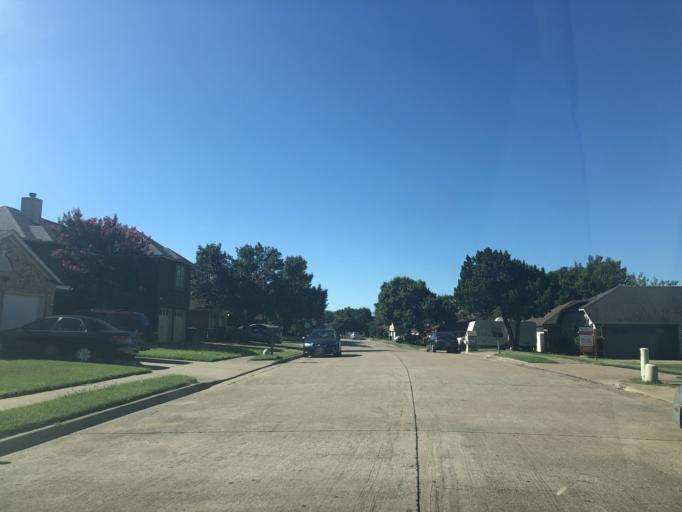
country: US
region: Texas
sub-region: Dallas County
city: Duncanville
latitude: 32.6664
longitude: -96.9353
